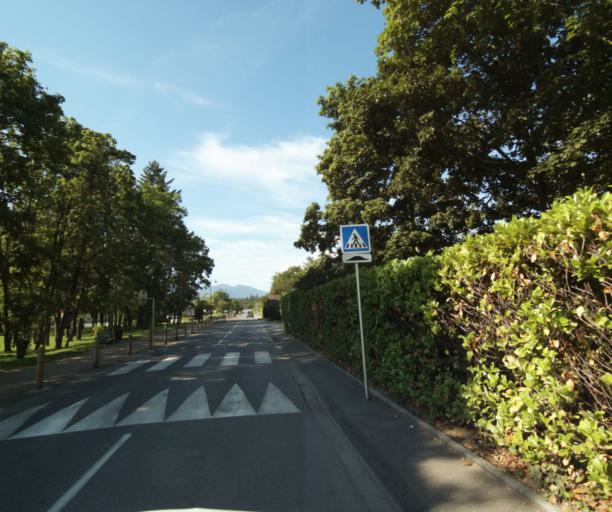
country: FR
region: Rhone-Alpes
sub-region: Departement de la Haute-Savoie
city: Marin
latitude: 46.3981
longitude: 6.5036
